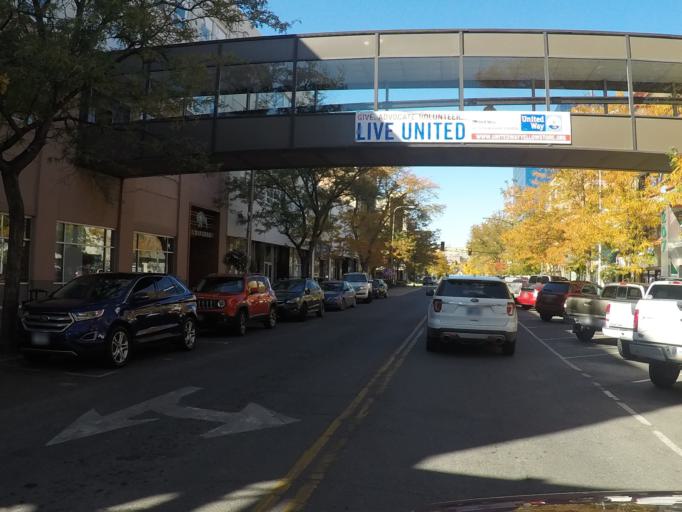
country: US
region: Montana
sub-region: Yellowstone County
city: Billings
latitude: 45.7831
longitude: -108.5068
